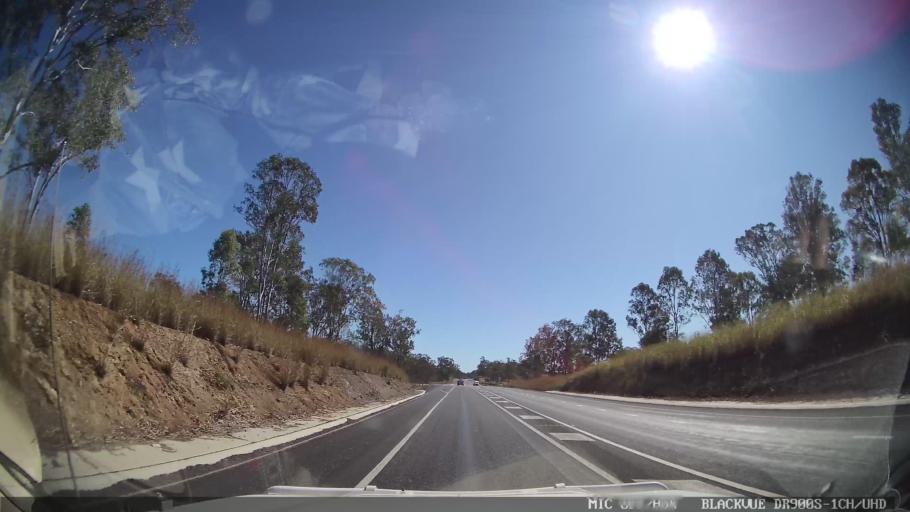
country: AU
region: Queensland
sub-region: Gympie Regional Council
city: Gympie
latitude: -26.0368
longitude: 152.5689
